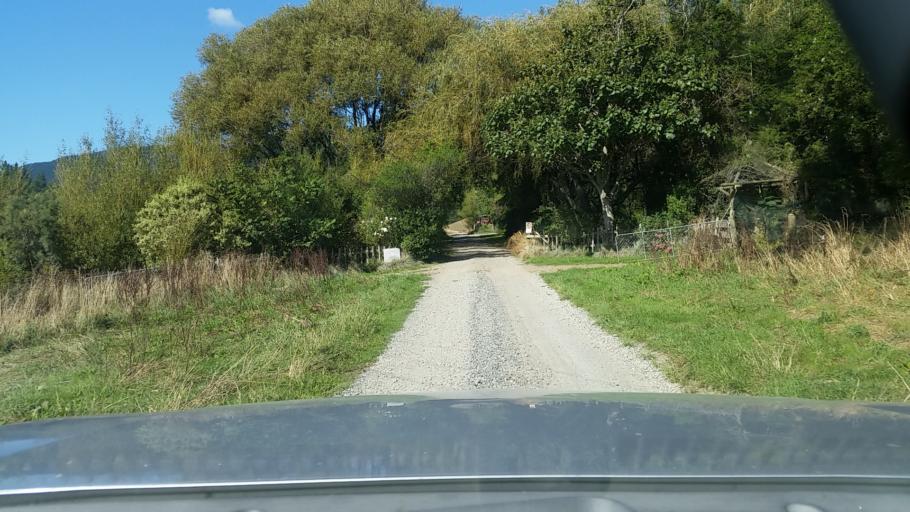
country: NZ
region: Marlborough
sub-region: Marlborough District
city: Blenheim
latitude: -41.4083
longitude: 173.7925
